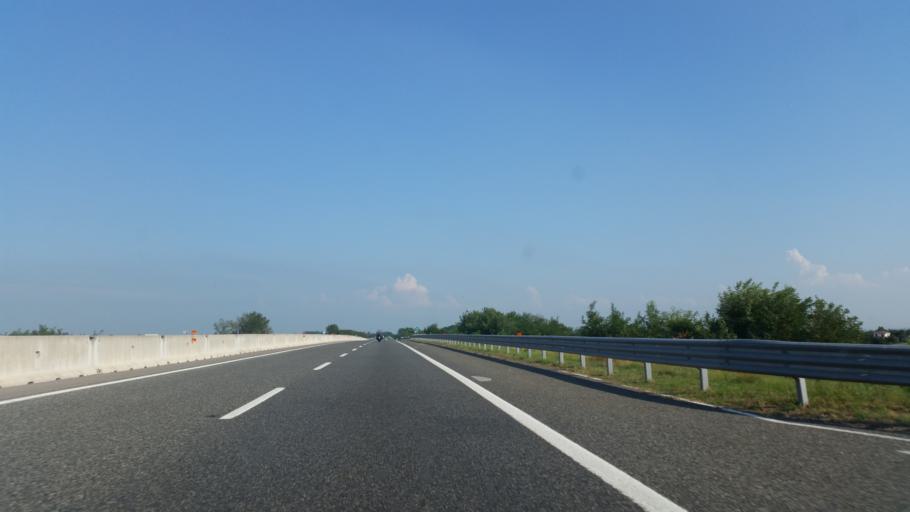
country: IT
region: Piedmont
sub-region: Provincia di Vercelli
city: Asigliano Vercellese
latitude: 45.2714
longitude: 8.4177
